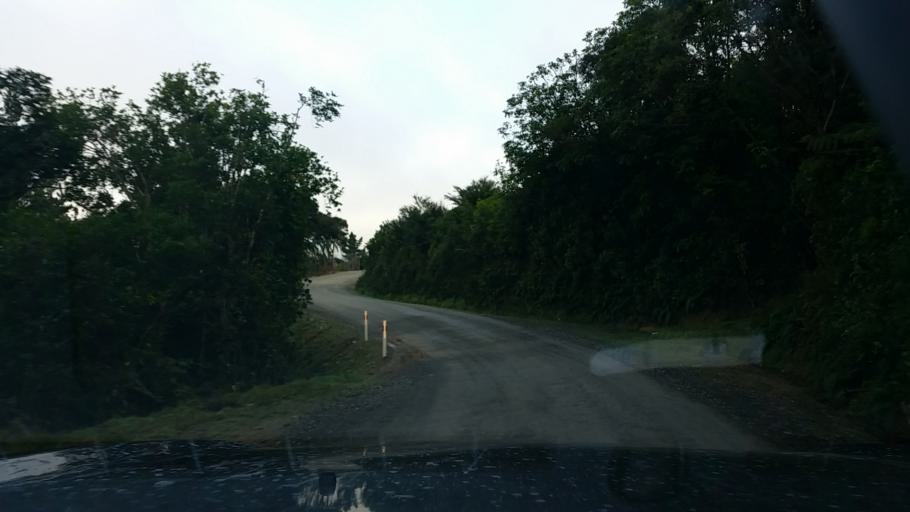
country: NZ
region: Marlborough
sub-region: Marlborough District
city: Picton
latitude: -41.1784
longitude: 174.0638
